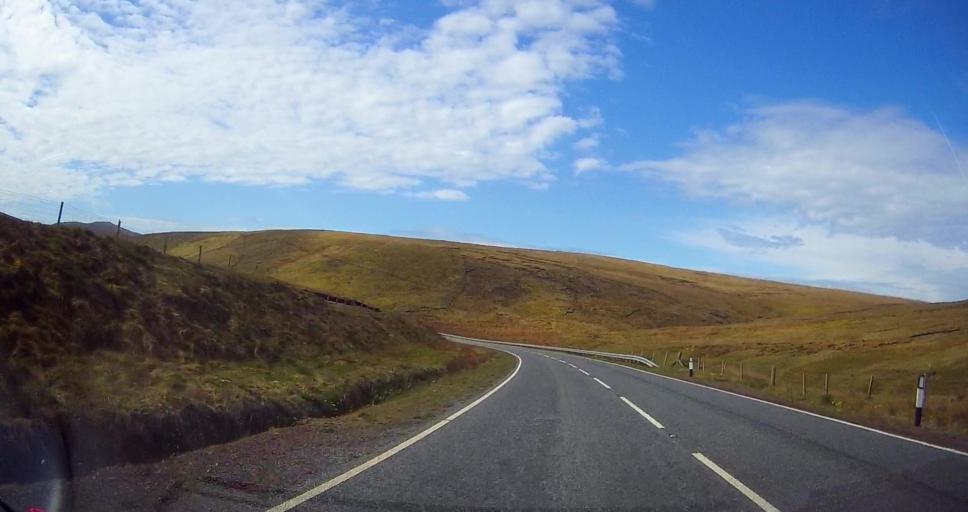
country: GB
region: Scotland
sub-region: Shetland Islands
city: Sandwick
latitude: 60.0066
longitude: -1.2752
